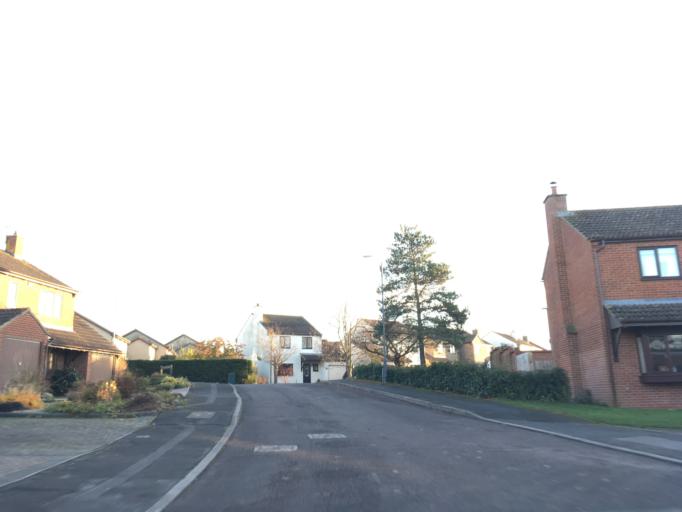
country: GB
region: England
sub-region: South Gloucestershire
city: Thornbury
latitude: 51.6151
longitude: -2.5109
